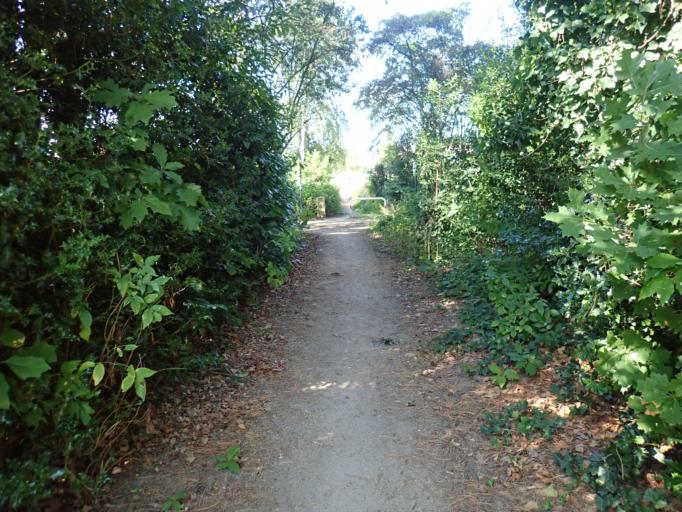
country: BE
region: Flanders
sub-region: Provincie Antwerpen
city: Westerlo
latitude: 51.1275
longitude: 4.9025
